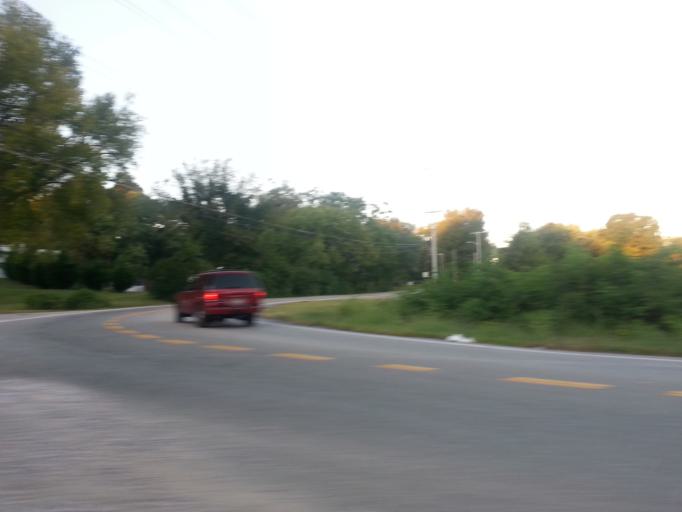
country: US
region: Tennessee
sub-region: Knox County
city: Knoxville
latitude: 35.9650
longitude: -83.8972
